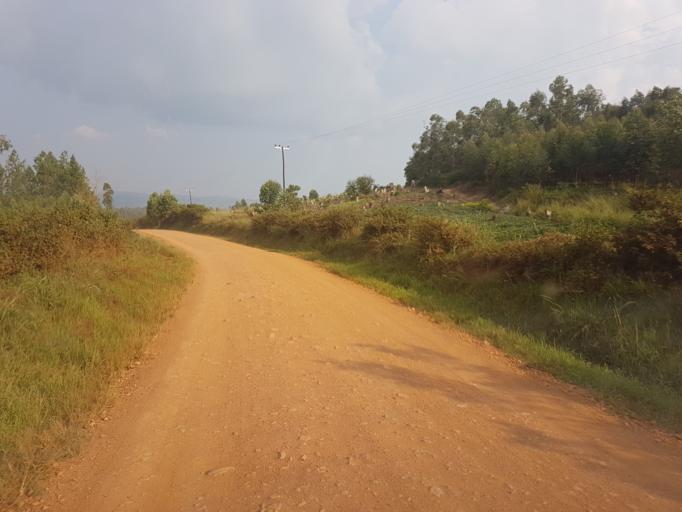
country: UG
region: Western Region
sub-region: Rukungiri District
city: Rukungiri
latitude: -0.6570
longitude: 29.8617
